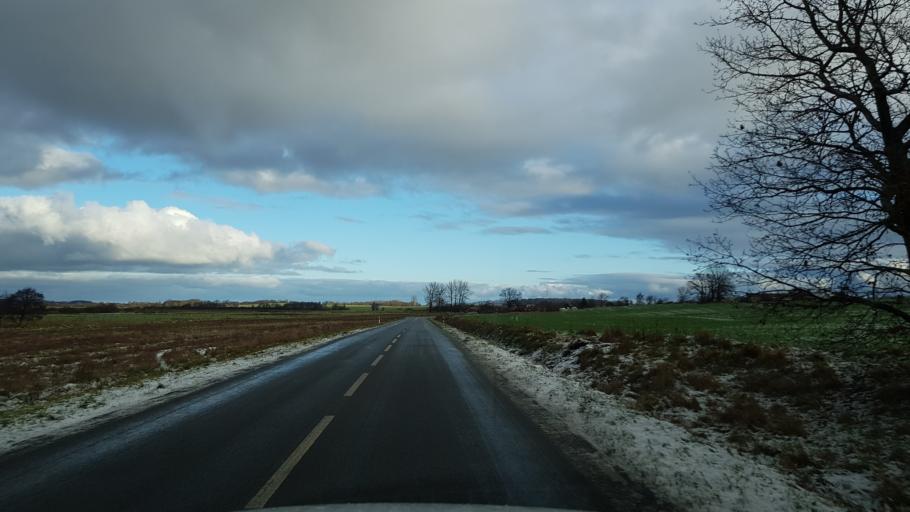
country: PL
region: West Pomeranian Voivodeship
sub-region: Powiat gryficki
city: Karnice
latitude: 54.0459
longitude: 15.0628
